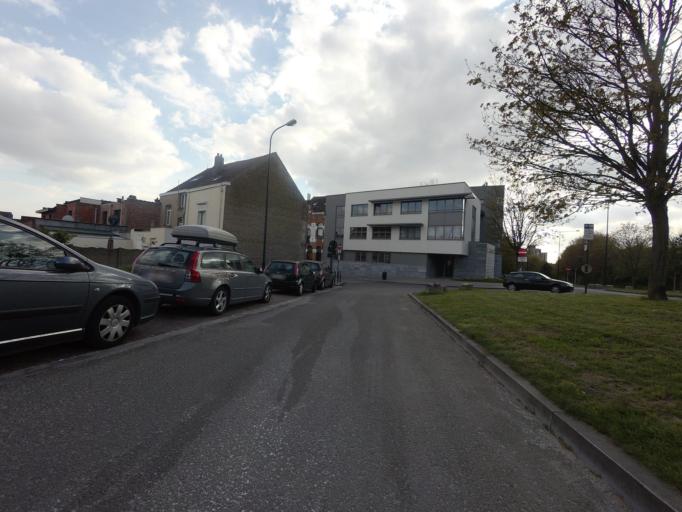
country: BE
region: Flanders
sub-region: Provincie Vlaams-Brabant
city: Grimbergen
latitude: 50.8964
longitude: 4.3838
